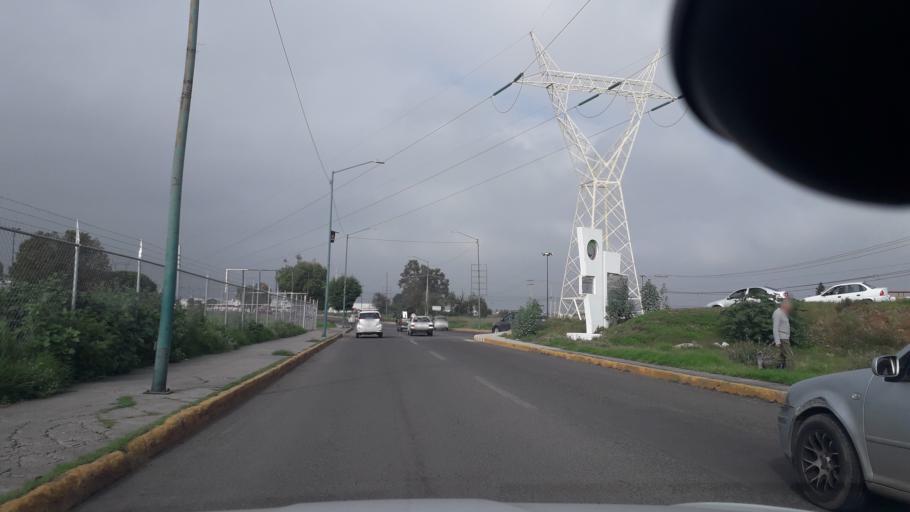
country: MX
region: Mexico
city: Coacalco
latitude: 19.6451
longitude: -99.1026
